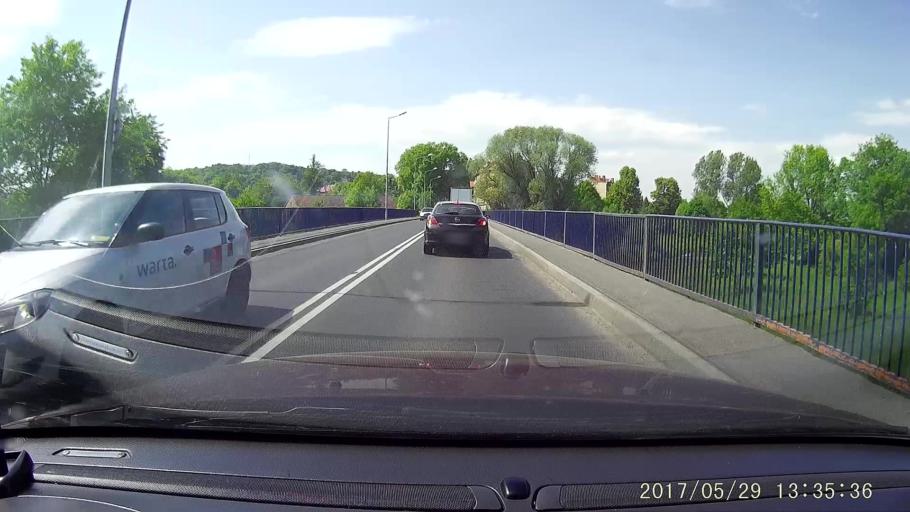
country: PL
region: Lower Silesian Voivodeship
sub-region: Powiat lubanski
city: Luban
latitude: 51.1105
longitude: 15.2980
